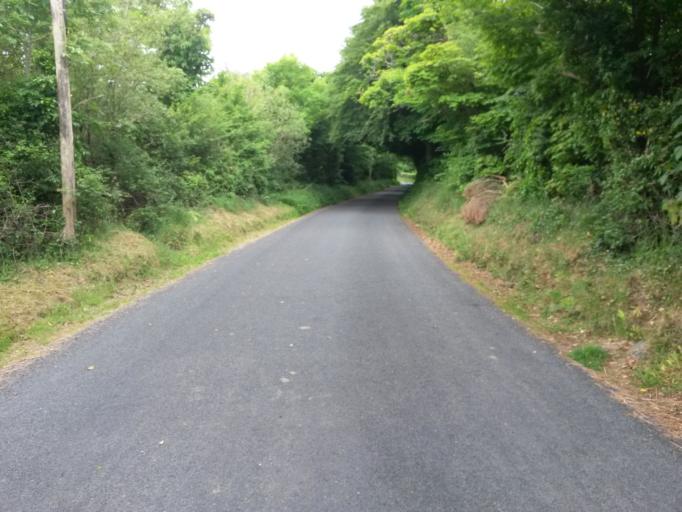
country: IE
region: Munster
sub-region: An Clar
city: Ennis
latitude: 52.9086
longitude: -9.0686
